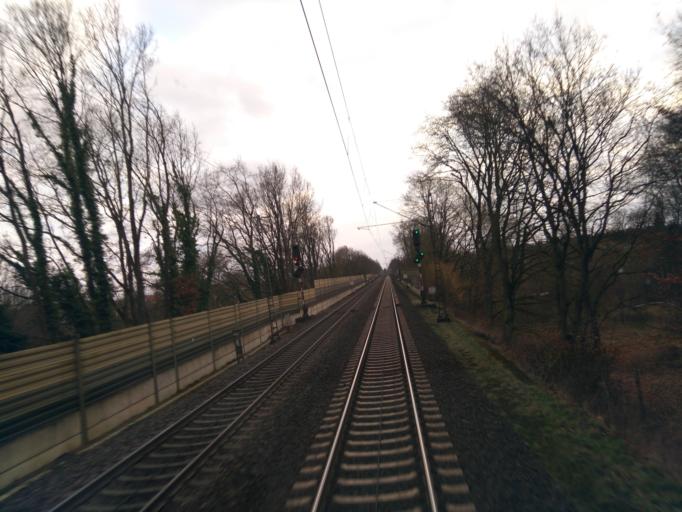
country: DE
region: Lower Saxony
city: Bad Bevensen
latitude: 53.0854
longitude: 10.5677
